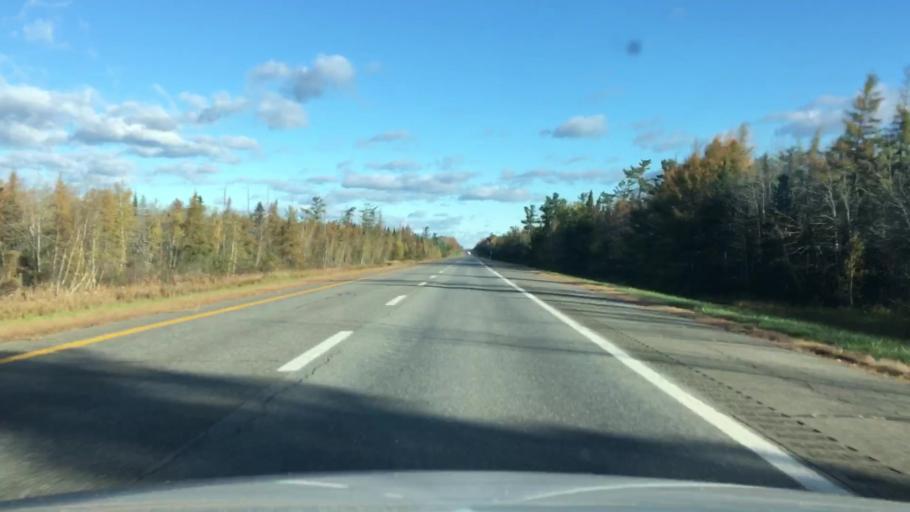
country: US
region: Maine
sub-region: Penobscot County
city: Greenbush
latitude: 45.0565
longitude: -68.6877
